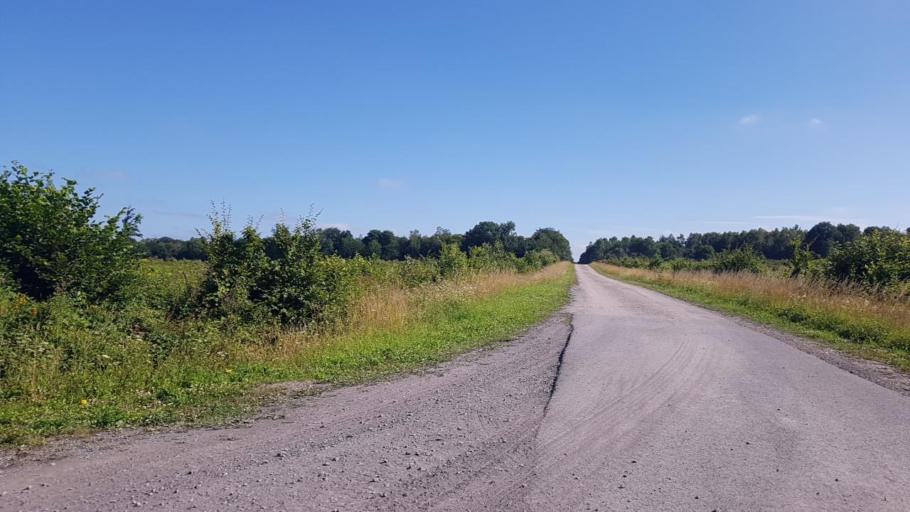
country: FR
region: Picardie
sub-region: Departement de l'Aisne
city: Hirson
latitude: 49.9463
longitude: 4.1010
